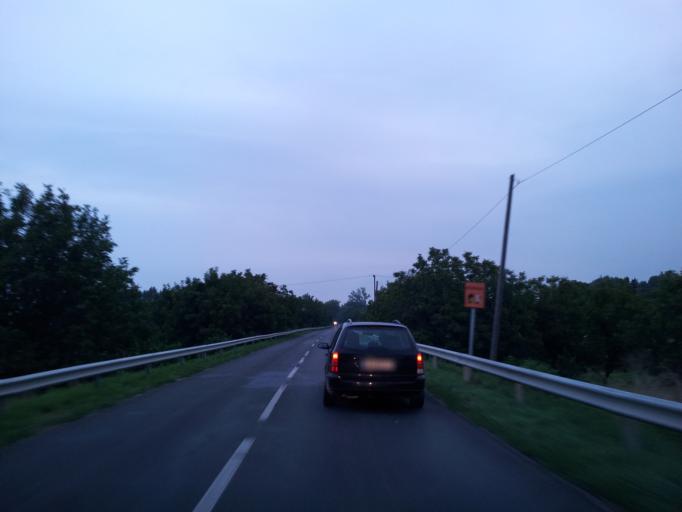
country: HU
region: Tolna
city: Tolna
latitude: 46.4258
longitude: 18.7937
